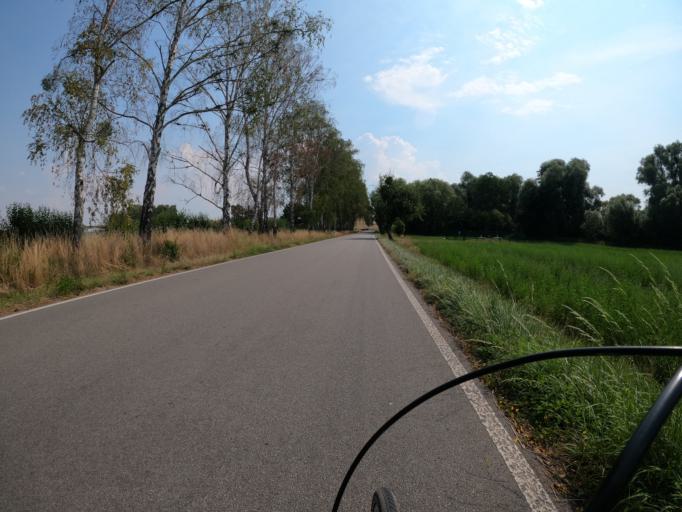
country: DE
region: Brandenburg
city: Angermunde
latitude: 53.0495
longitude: 13.9551
